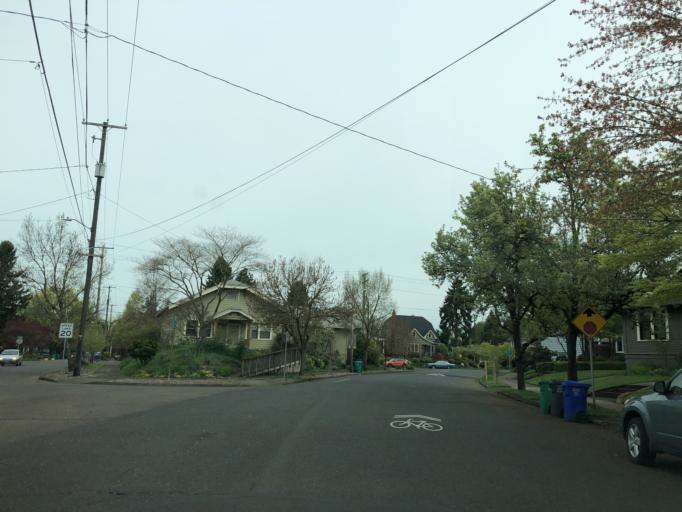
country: US
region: Oregon
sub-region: Multnomah County
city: Portland
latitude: 45.5523
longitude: -122.6337
